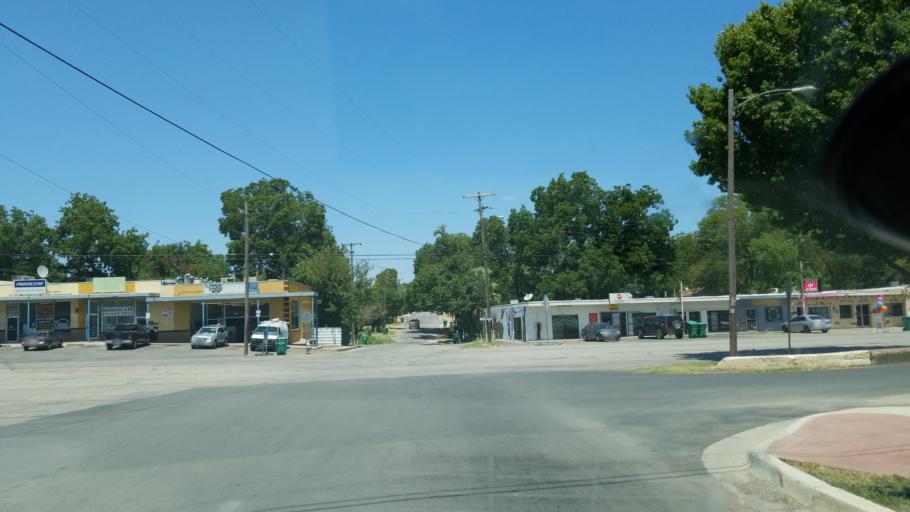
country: US
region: Texas
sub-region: Dallas County
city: Cockrell Hill
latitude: 32.7380
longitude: -96.8872
